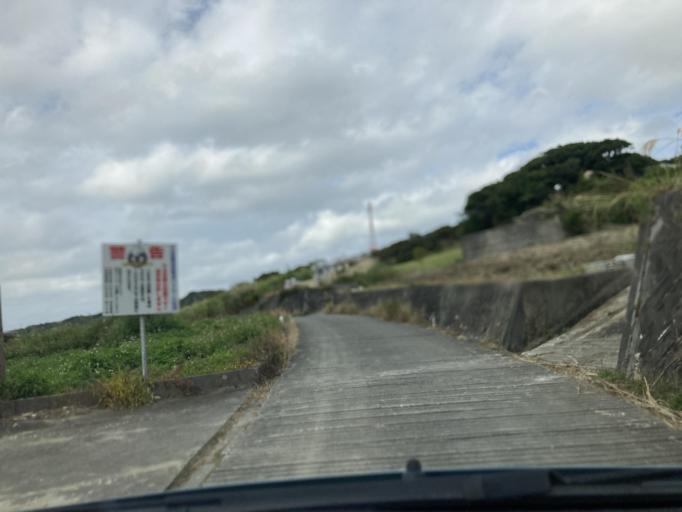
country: JP
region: Okinawa
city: Ginowan
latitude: 26.2129
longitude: 127.7437
